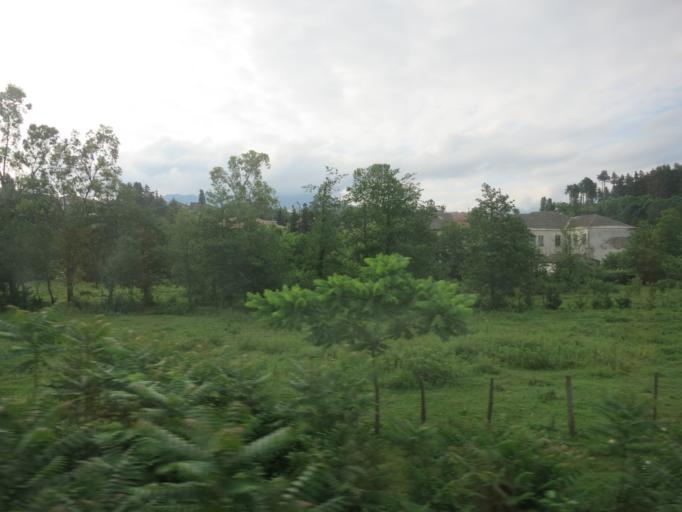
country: GE
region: Ajaria
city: Makhinjauri
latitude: 41.7444
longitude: 41.7378
